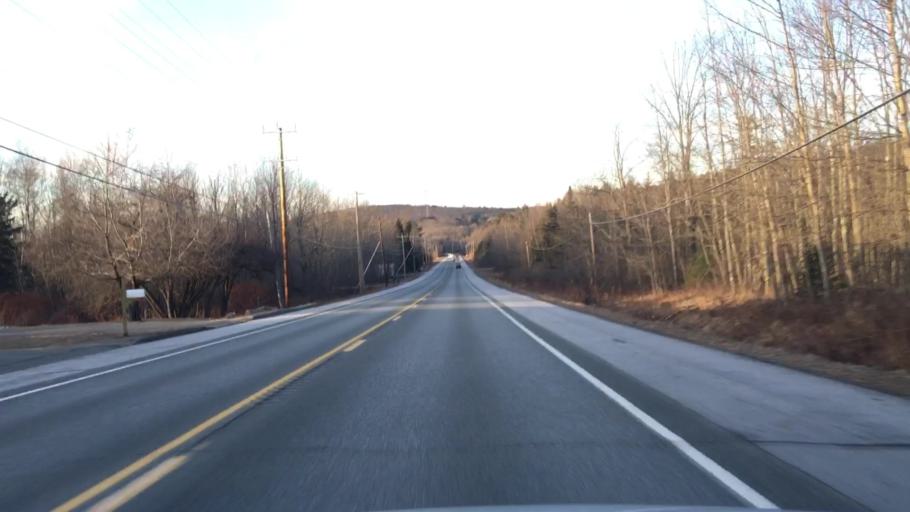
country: US
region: Maine
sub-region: Hancock County
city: Dedham
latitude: 44.7067
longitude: -68.6007
